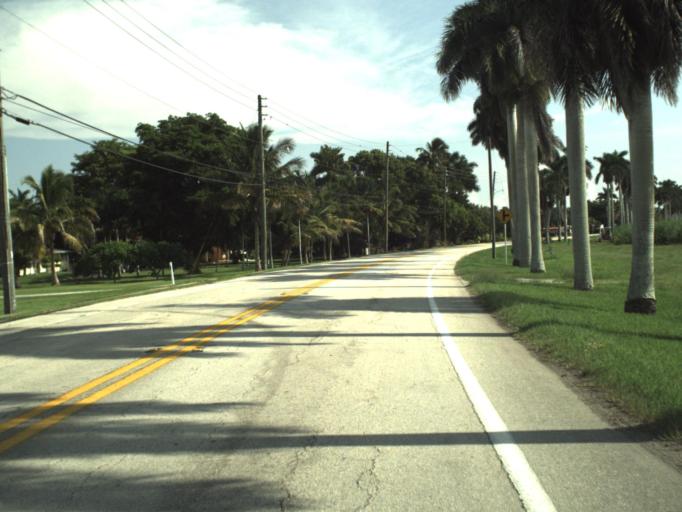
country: US
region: Florida
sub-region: Palm Beach County
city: Pahokee
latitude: 26.8039
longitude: -80.6931
